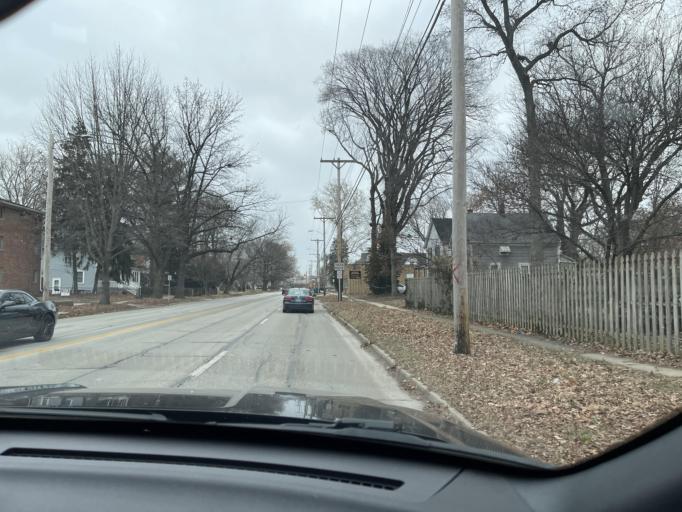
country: US
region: Illinois
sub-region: Sangamon County
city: Springfield
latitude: 39.7942
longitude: -89.6629
